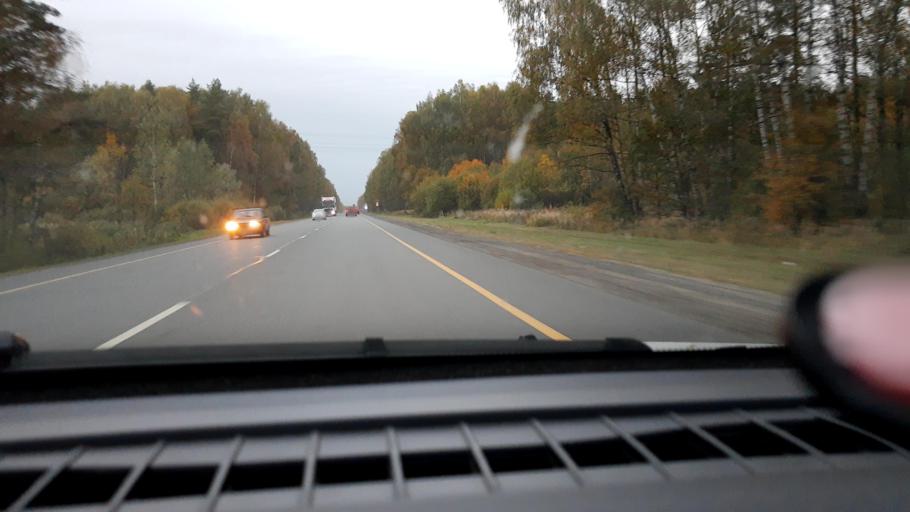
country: RU
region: Vladimir
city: Orgtrud
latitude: 56.2100
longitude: 40.6226
